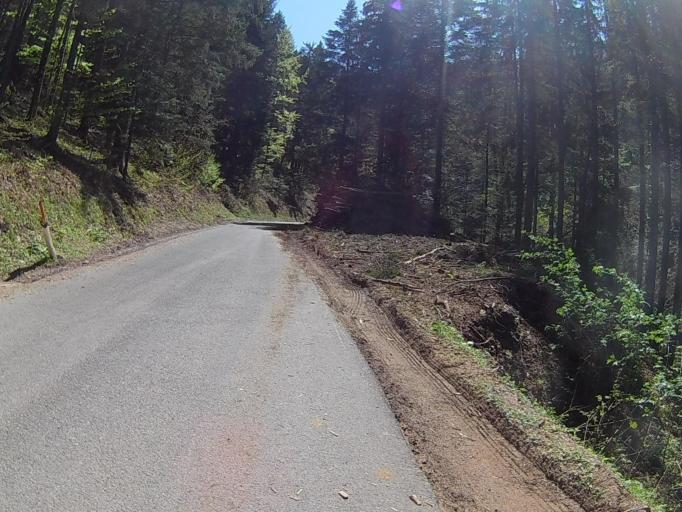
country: SI
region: Ruse
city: Ruse
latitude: 46.5312
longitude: 15.5127
